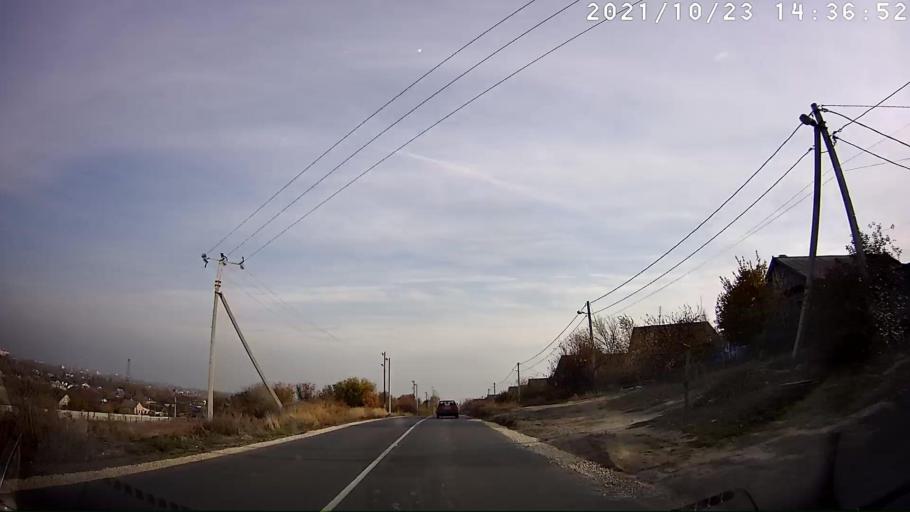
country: RU
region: Volgograd
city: Krasnoslobodsk
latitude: 48.5006
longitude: 44.5445
